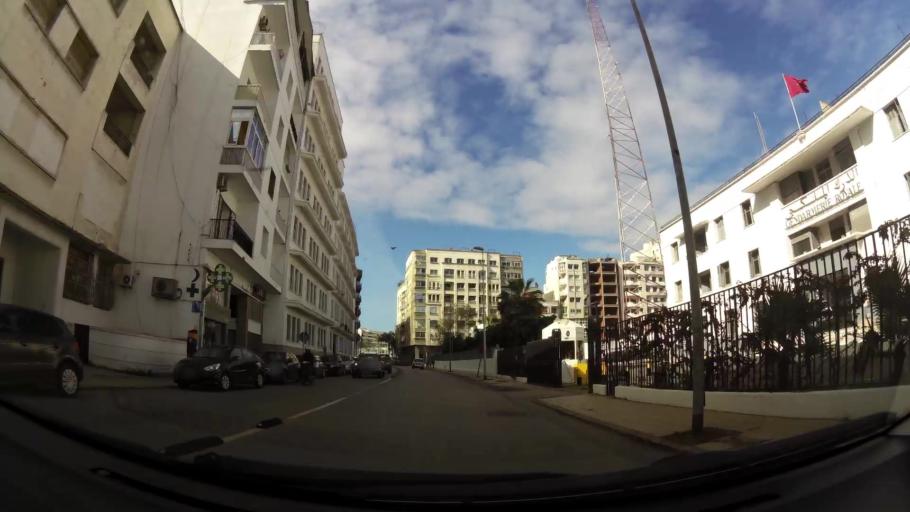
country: MA
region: Grand Casablanca
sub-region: Casablanca
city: Casablanca
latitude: 33.5851
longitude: -7.6241
